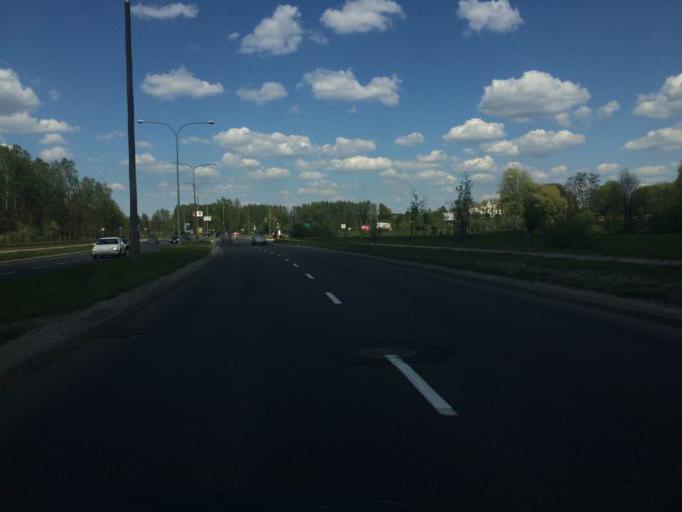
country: PL
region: Warmian-Masurian Voivodeship
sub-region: Olsztyn
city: Kortowo
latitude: 53.7729
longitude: 20.4494
